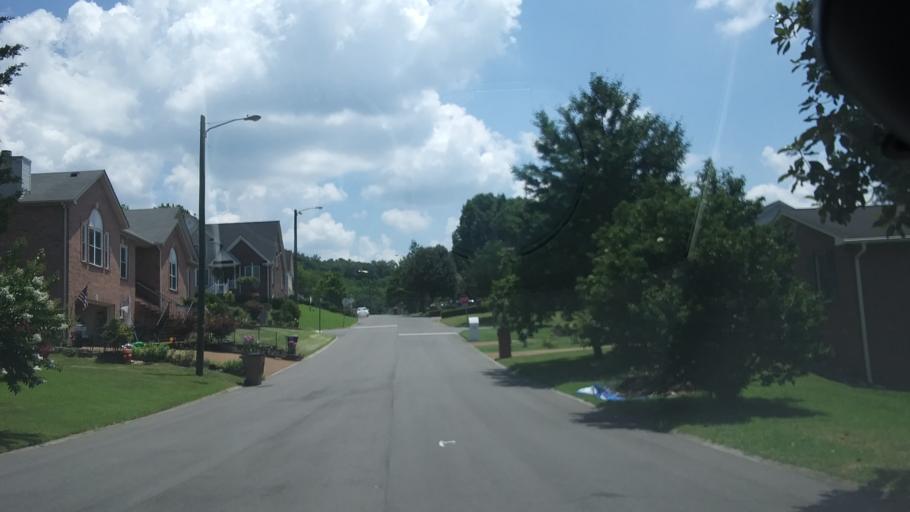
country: US
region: Tennessee
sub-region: Davidson County
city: Belle Meade
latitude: 36.1186
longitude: -86.9190
